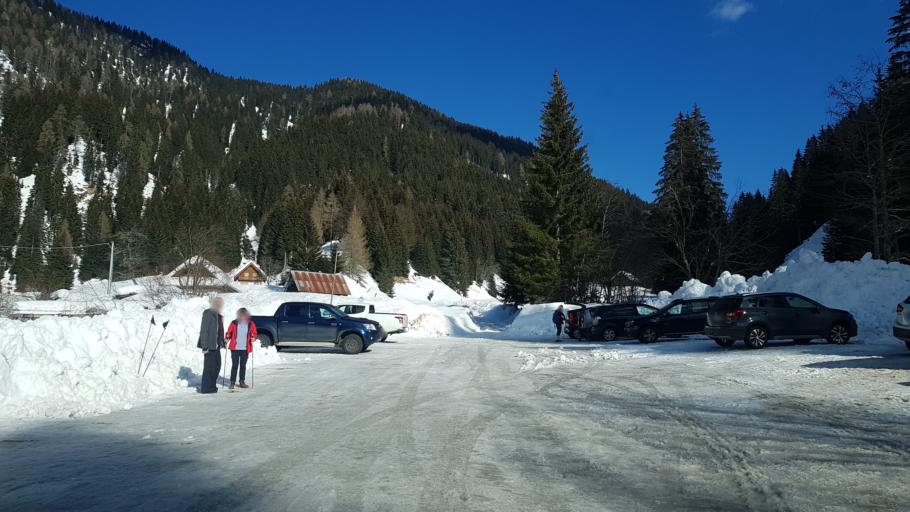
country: IT
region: Friuli Venezia Giulia
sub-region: Provincia di Udine
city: Malborghetto
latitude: 46.5496
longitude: 13.4814
